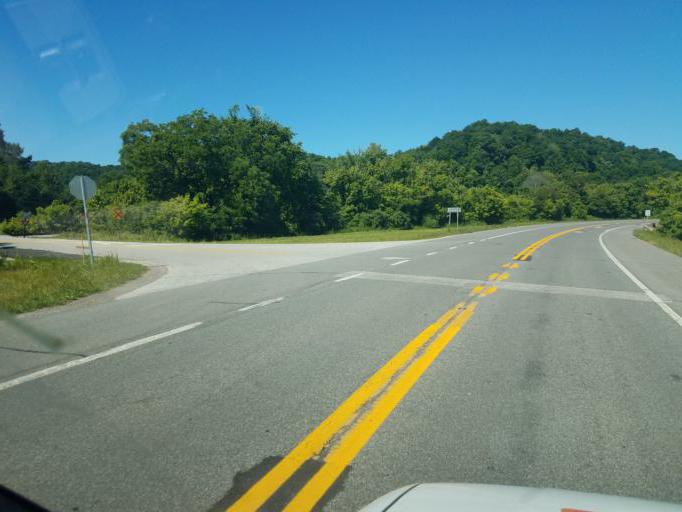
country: US
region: West Virginia
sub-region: Cabell County
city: Lesage
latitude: 38.5842
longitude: -82.2273
